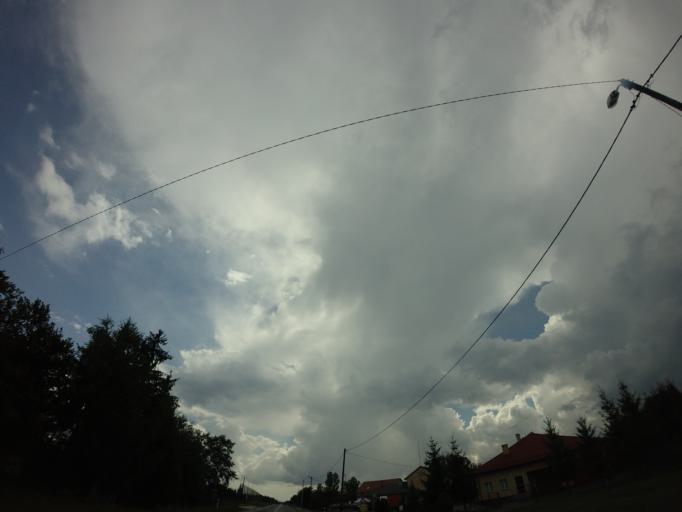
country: PL
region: Swietokrzyskie
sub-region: Powiat staszowski
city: Olesnica
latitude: 50.4746
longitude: 21.0304
